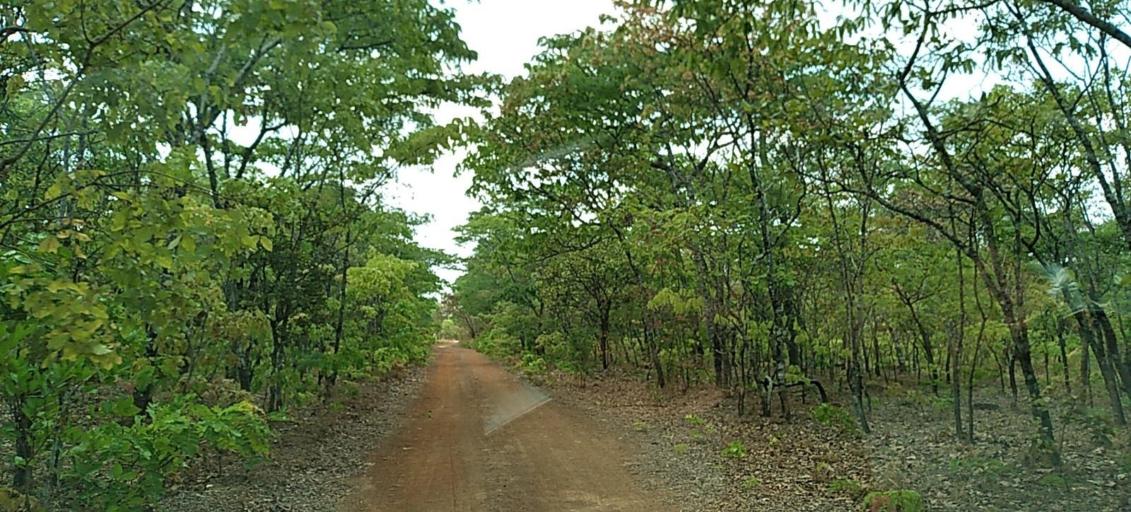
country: ZM
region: Copperbelt
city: Chililabombwe
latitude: -12.4949
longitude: 27.6375
